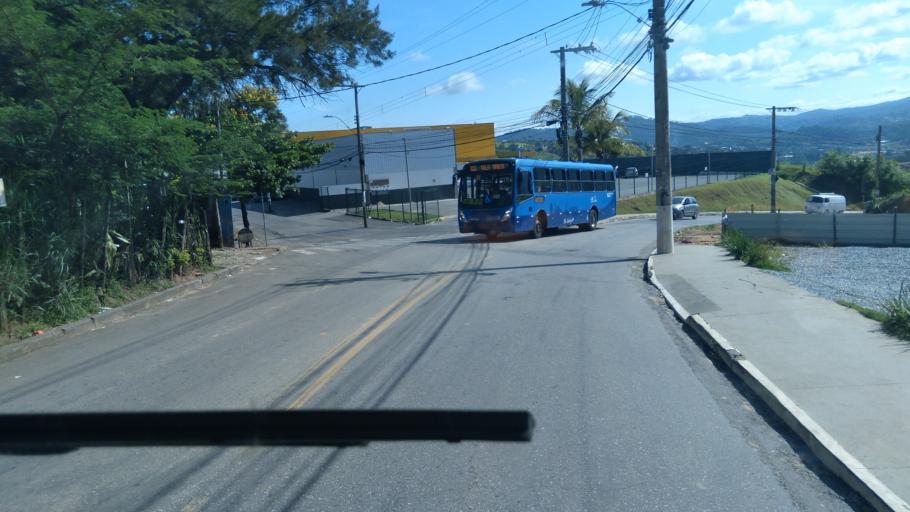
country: BR
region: Minas Gerais
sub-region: Santa Luzia
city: Santa Luzia
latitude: -19.8461
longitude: -43.8848
